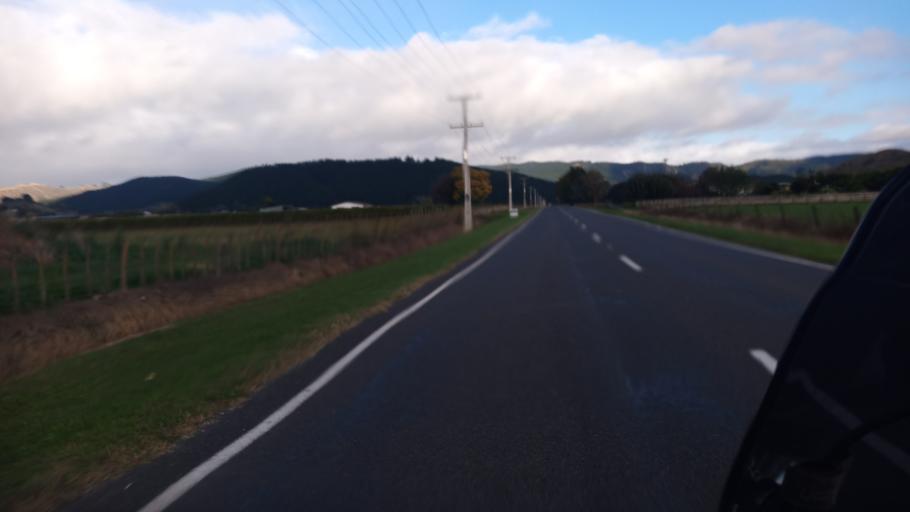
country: NZ
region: Gisborne
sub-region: Gisborne District
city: Gisborne
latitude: -38.6333
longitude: 177.8685
